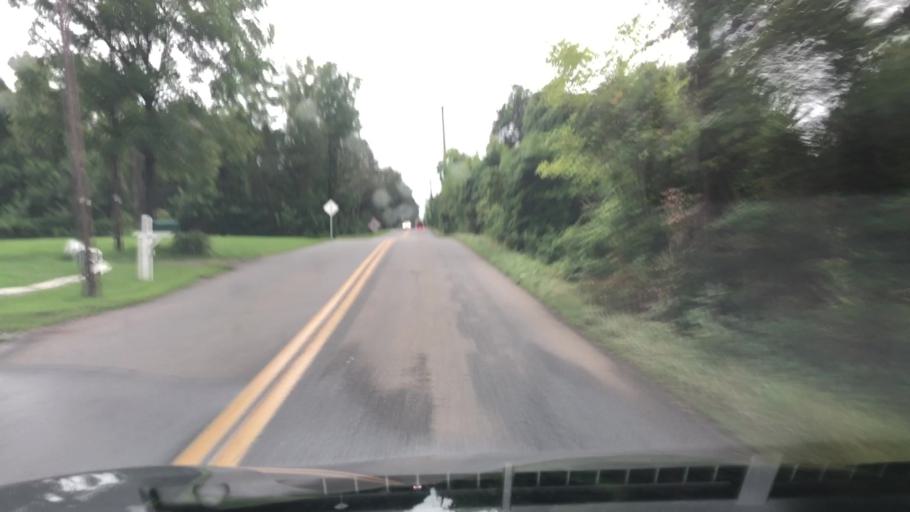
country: US
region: Virginia
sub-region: Prince William County
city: Nokesville
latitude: 38.6622
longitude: -77.6453
